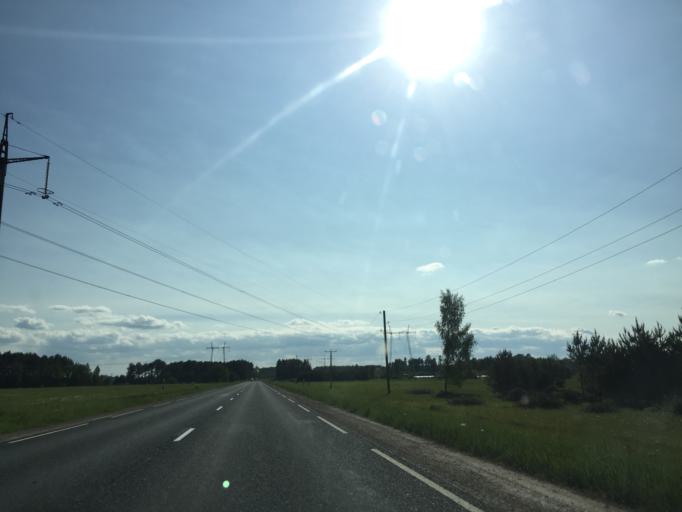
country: LV
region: Kekava
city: Kekava
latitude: 56.8206
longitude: 24.2999
